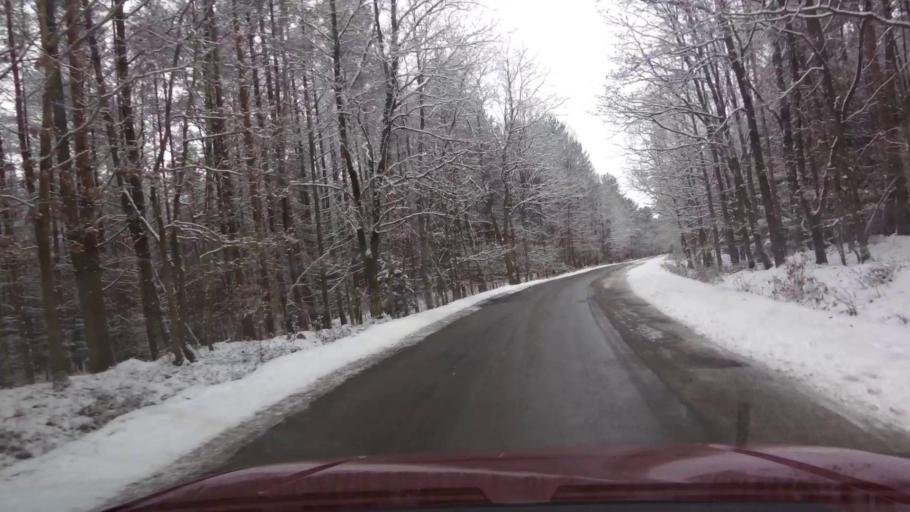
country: PL
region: West Pomeranian Voivodeship
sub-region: Powiat swidwinski
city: Rabino
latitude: 53.9190
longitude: 15.9543
